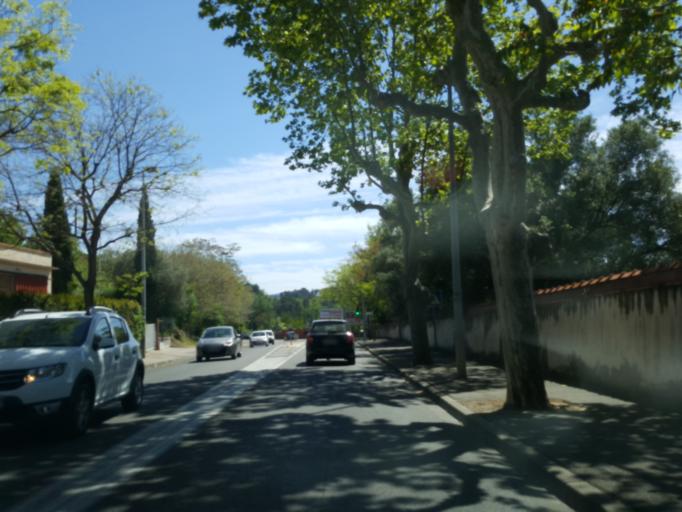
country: FR
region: Provence-Alpes-Cote d'Azur
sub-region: Departement des Bouches-du-Rhone
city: Roquevaire
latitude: 43.3459
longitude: 5.6034
